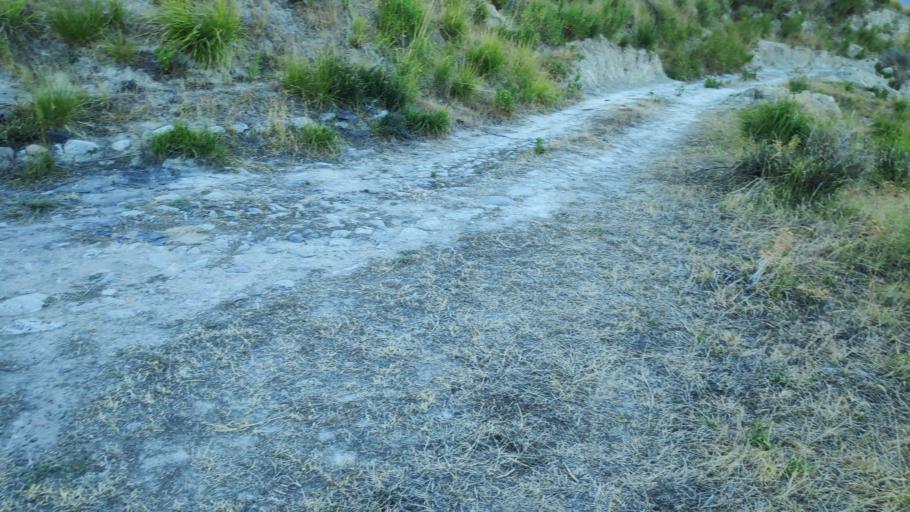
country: IT
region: Calabria
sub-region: Provincia di Reggio Calabria
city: Stilo
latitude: 38.4952
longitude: 16.4763
